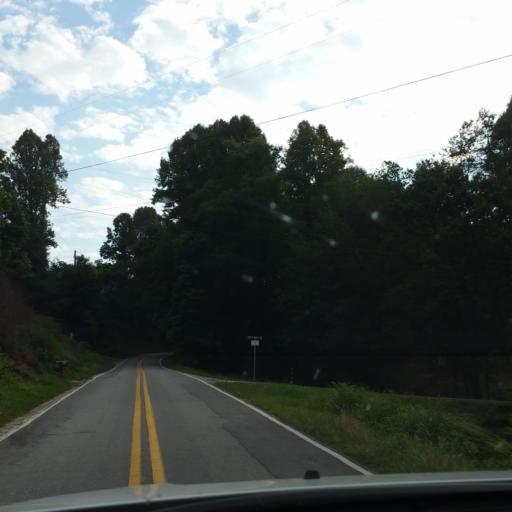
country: US
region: North Carolina
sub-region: Buncombe County
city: Bent Creek
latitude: 35.5220
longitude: -82.6855
